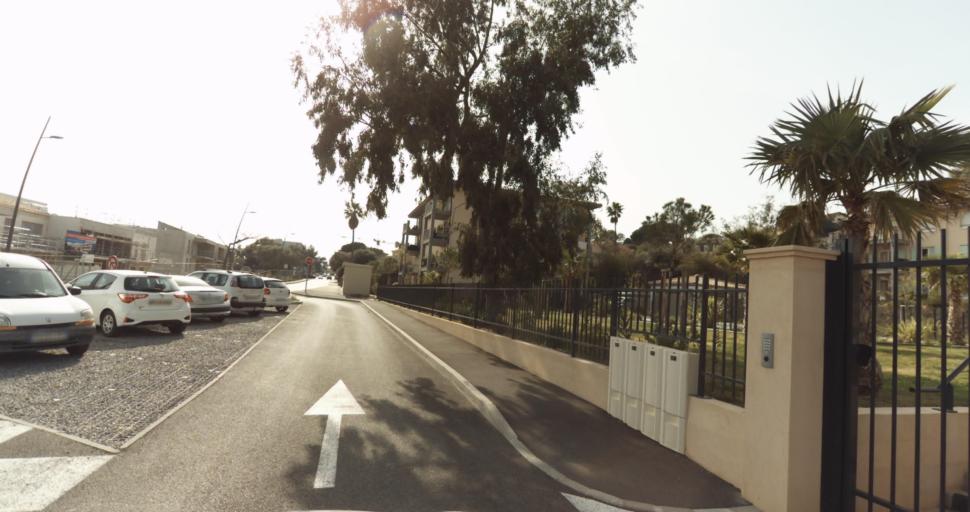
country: FR
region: Provence-Alpes-Cote d'Azur
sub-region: Departement du Var
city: Bormes-les-Mimosas
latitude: 43.1461
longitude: 6.3427
